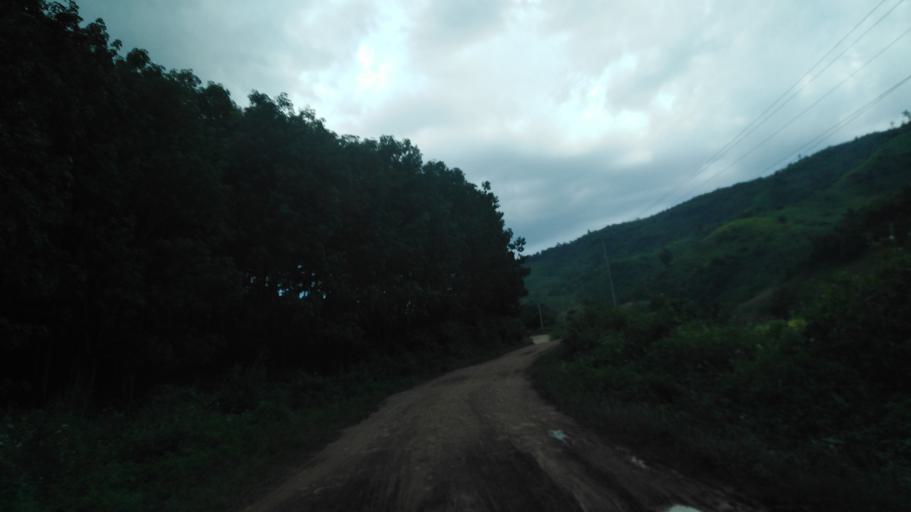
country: TH
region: Nan
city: Song Khwae
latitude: 19.7335
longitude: 100.7275
